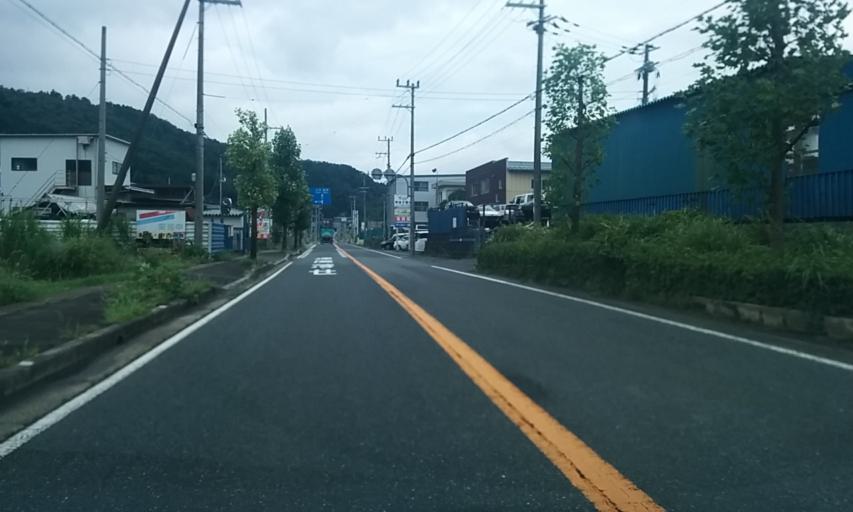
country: JP
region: Kyoto
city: Maizuru
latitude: 35.4491
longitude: 135.2629
